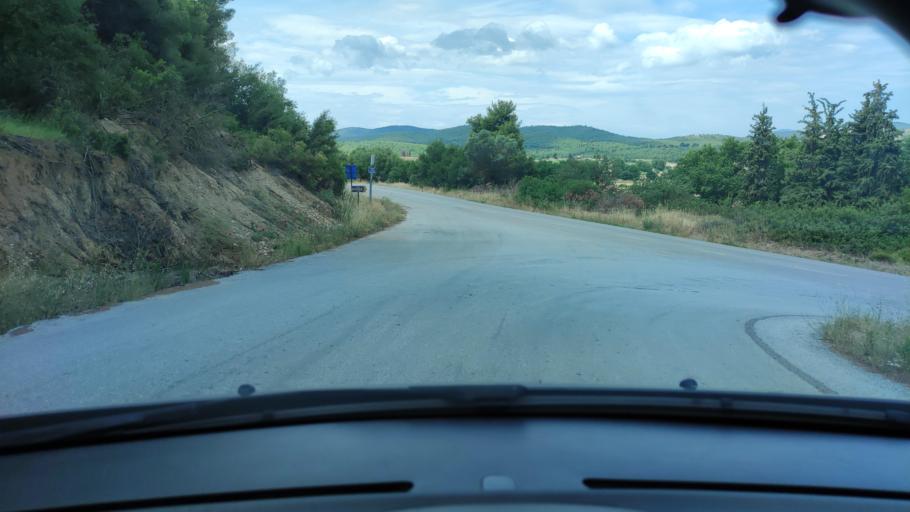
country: GR
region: Central Greece
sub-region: Nomos Evvoias
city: Afration
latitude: 38.5175
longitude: 23.7505
